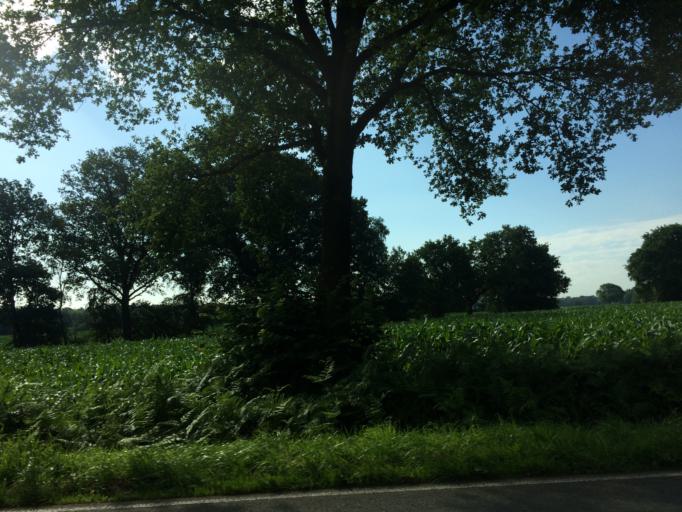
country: DE
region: North Rhine-Westphalia
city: Dorsten
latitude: 51.6995
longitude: 7.0047
